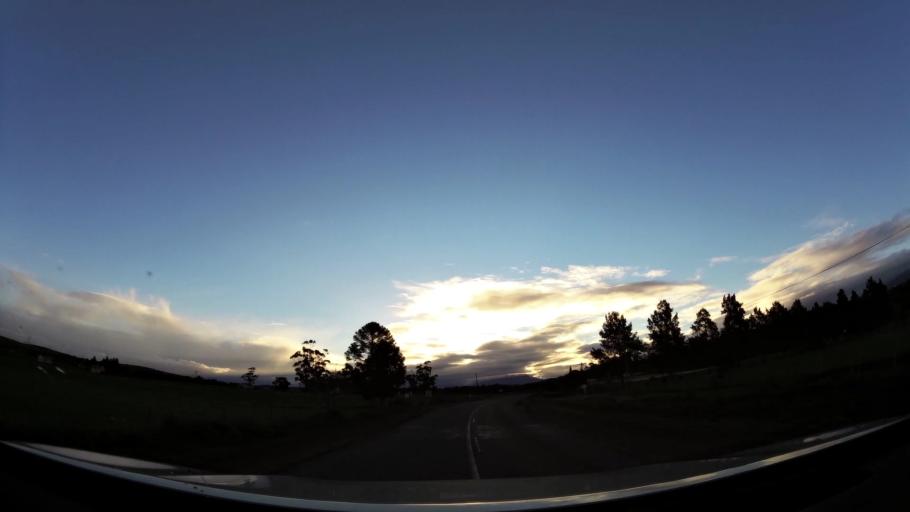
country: ZA
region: Western Cape
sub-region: Eden District Municipality
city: Riversdale
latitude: -34.0788
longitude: 20.9240
